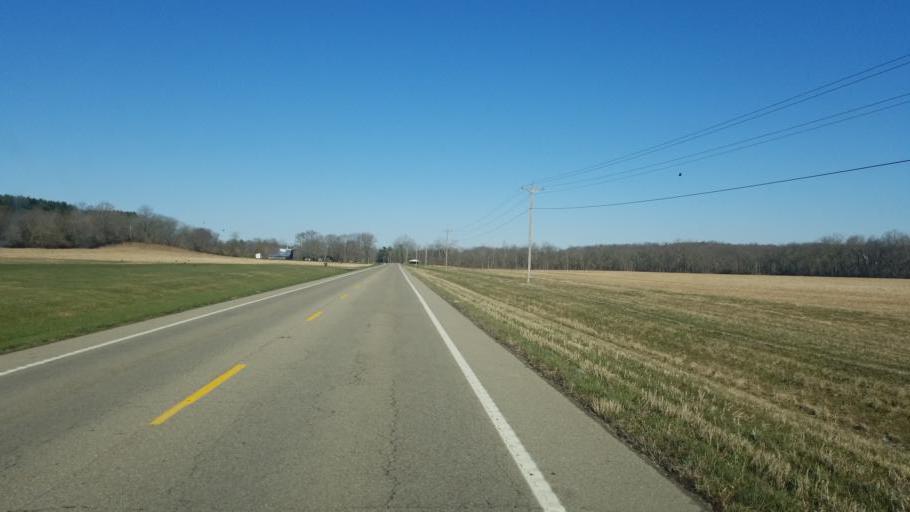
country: US
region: Ohio
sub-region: Highland County
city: Greenfield
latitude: 39.2272
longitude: -83.3187
